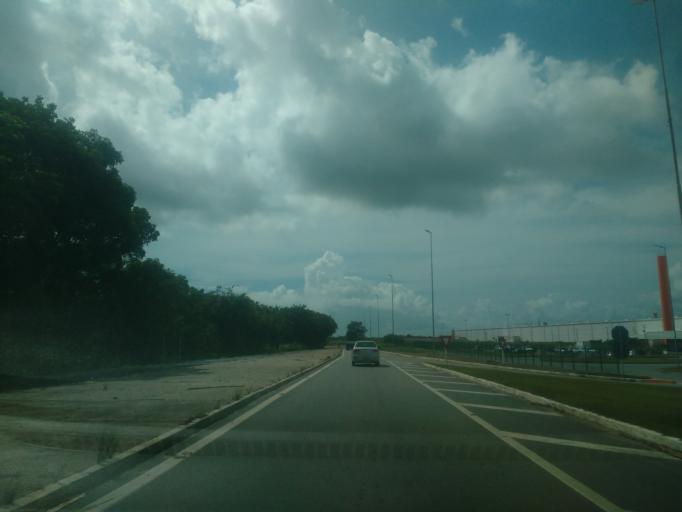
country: BR
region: Alagoas
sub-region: Marechal Deodoro
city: Marechal Deodoro
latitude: -9.6844
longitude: -35.8273
